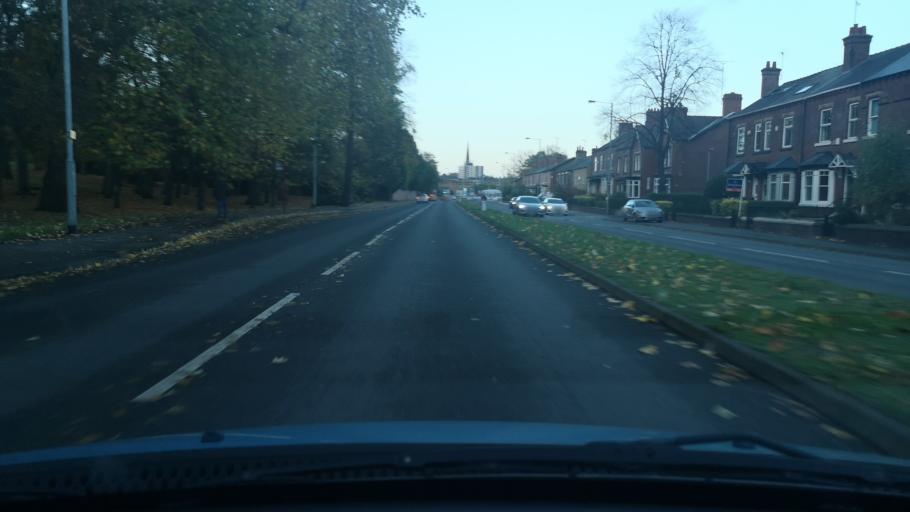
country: GB
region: England
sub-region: City and Borough of Wakefield
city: Wakefield
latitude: 53.6734
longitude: -1.5026
